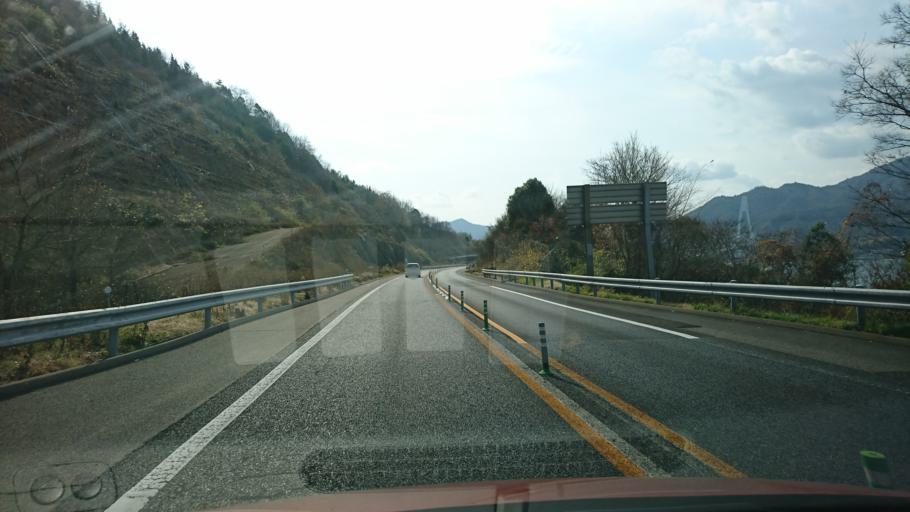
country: JP
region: Hiroshima
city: Innoshima
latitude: 34.3119
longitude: 133.1558
